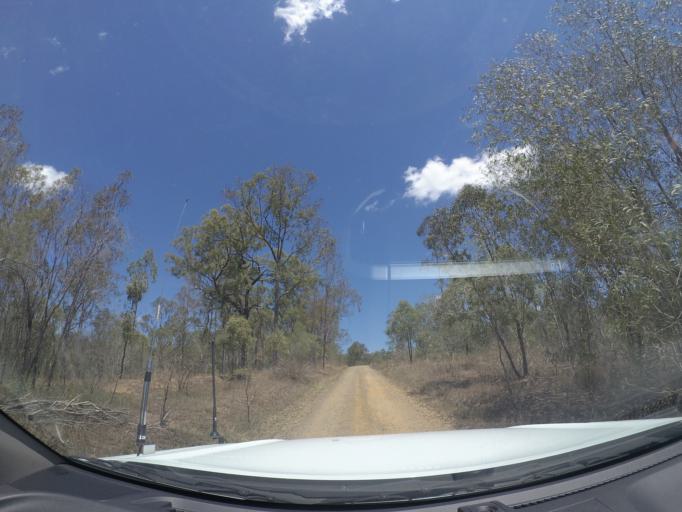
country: AU
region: Queensland
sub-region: Ipswich
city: Springfield Lakes
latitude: -27.8235
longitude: 152.8413
